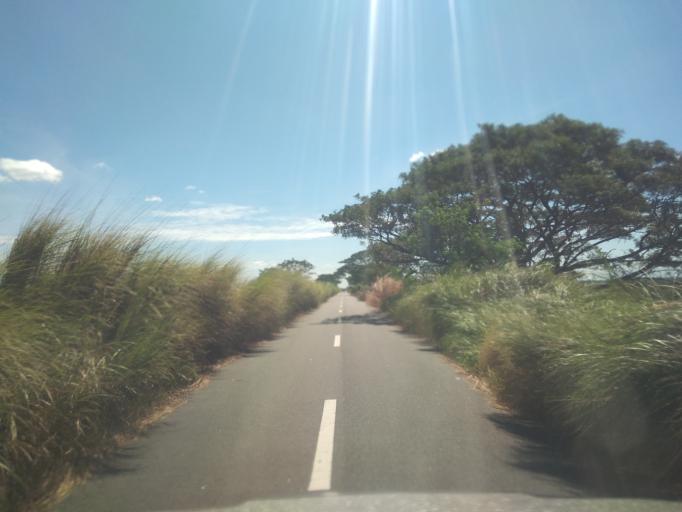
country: PH
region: Central Luzon
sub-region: Province of Pampanga
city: San Basilio
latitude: 15.0352
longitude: 120.5965
